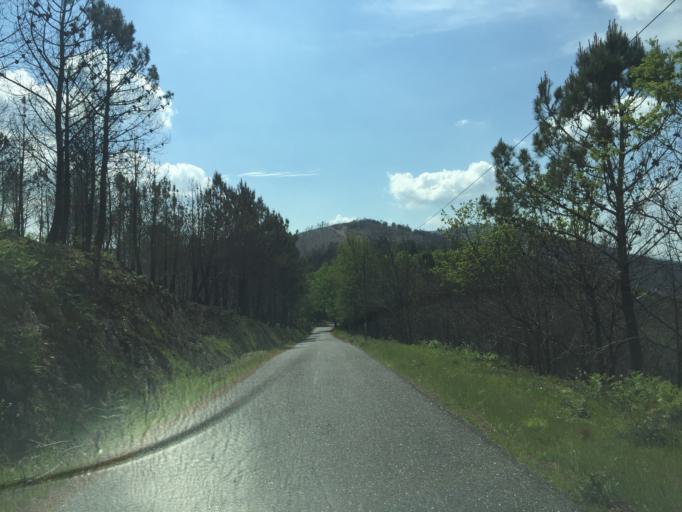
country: PT
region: Coimbra
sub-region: Arganil
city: Arganil
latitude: 40.1853
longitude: -7.9732
